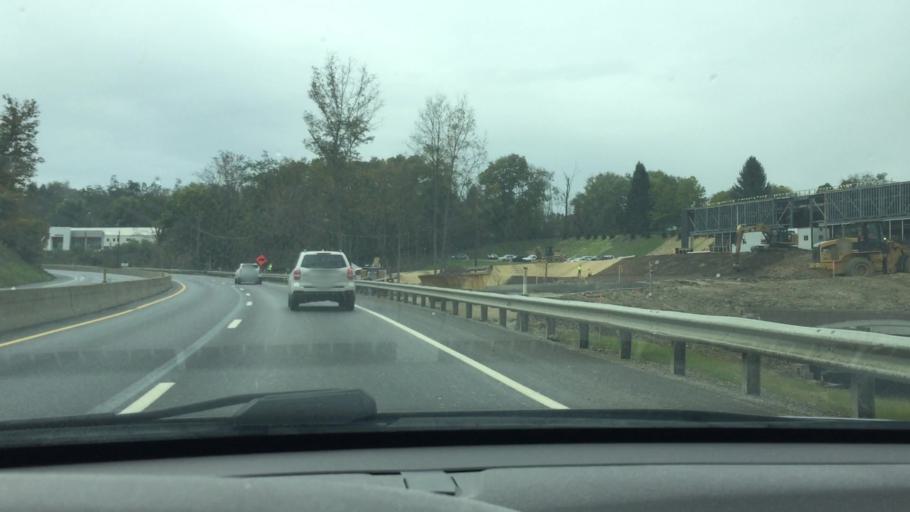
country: US
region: Pennsylvania
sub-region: Washington County
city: Canonsburg
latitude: 40.2552
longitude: -80.1668
